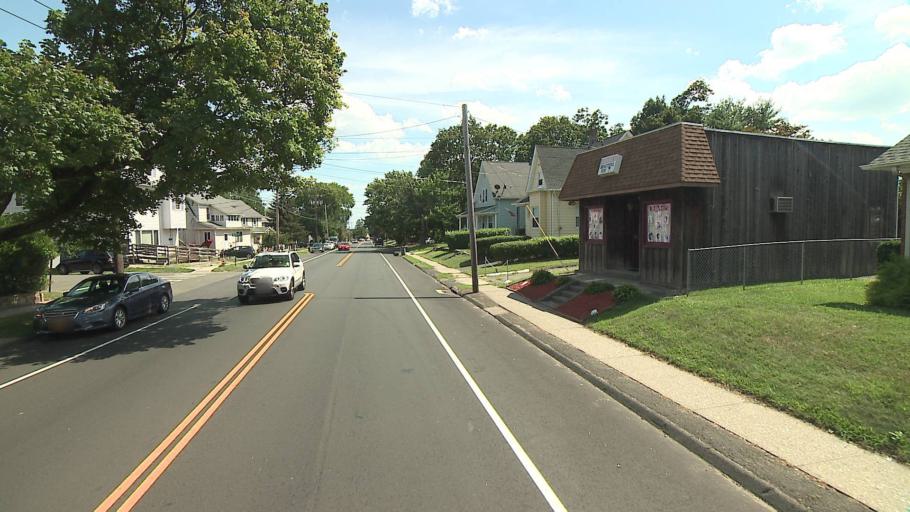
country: US
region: Connecticut
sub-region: Fairfield County
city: Stratford
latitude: 41.2020
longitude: -73.1395
